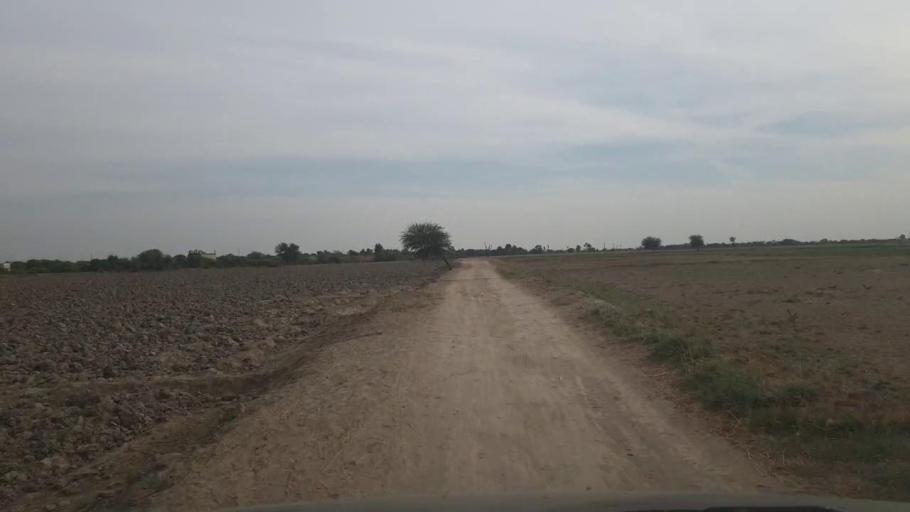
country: PK
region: Sindh
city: Kunri
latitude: 25.2810
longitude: 69.5998
